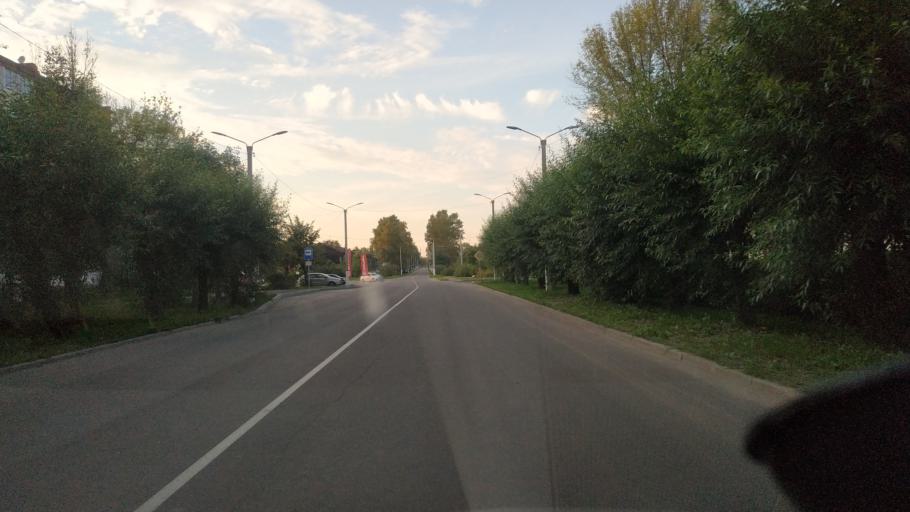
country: RU
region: Moskovskaya
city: Roshal'
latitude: 55.6655
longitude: 39.8526
